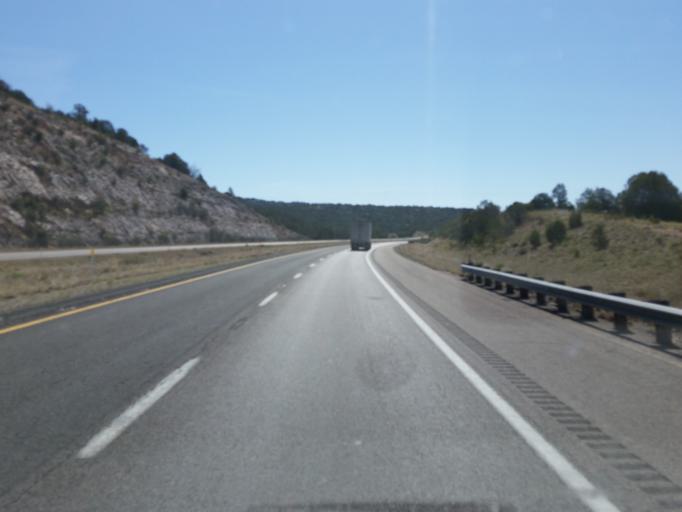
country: US
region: Arizona
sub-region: Mohave County
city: Peach Springs
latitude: 35.2874
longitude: -113.1129
